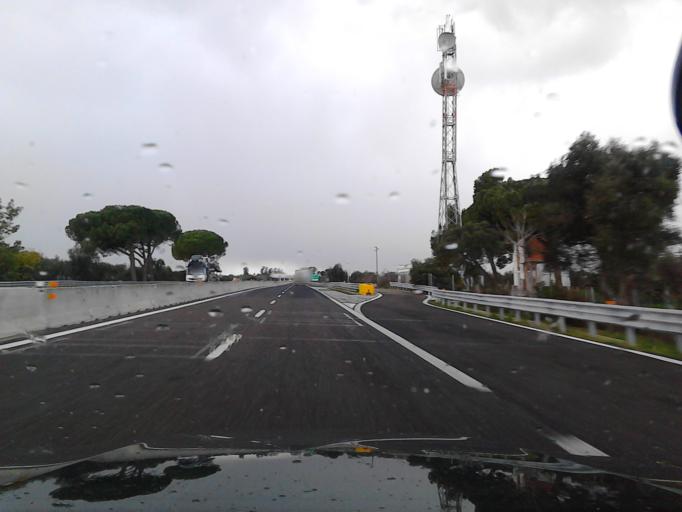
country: IT
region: Apulia
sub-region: Provincia di Bari
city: Bitonto
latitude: 41.1372
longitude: 16.7008
